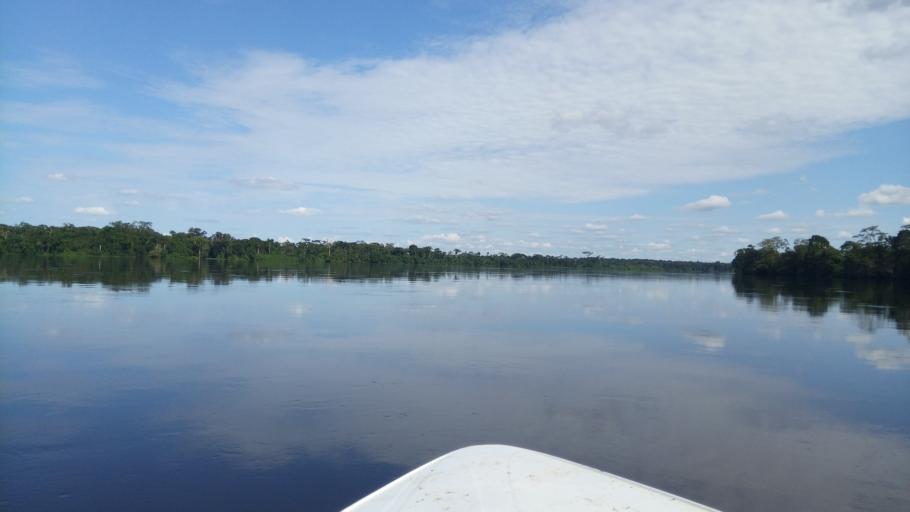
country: CD
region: Eastern Province
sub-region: Sous-Region de la Tshopo
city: Yangambi
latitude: 0.5494
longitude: 24.2461
